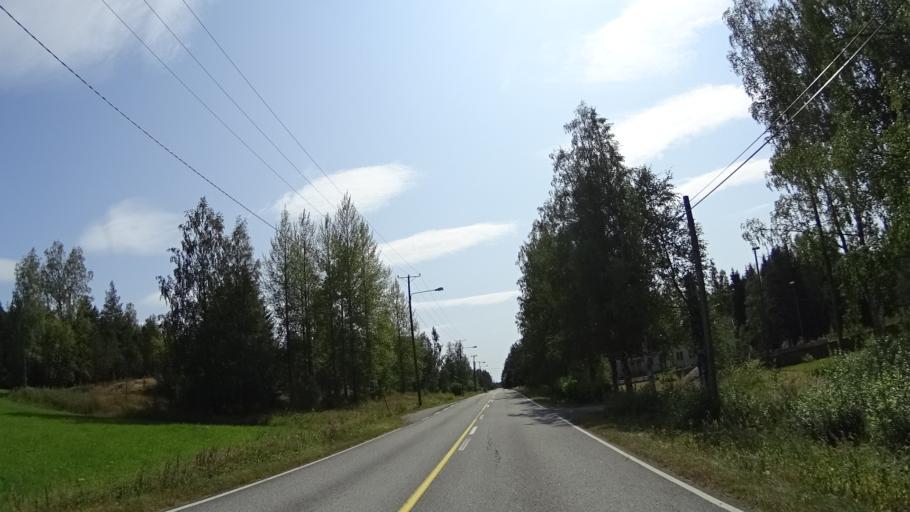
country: FI
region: Pirkanmaa
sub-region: Ylae-Pirkanmaa
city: Maenttae
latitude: 61.9075
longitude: 24.7861
